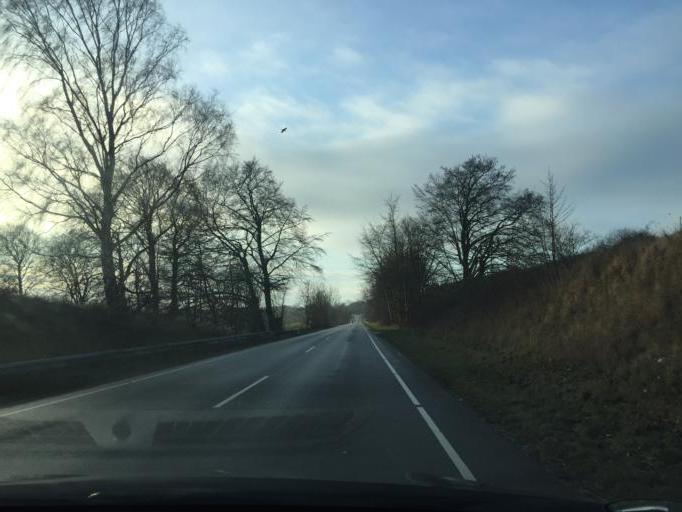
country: DK
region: South Denmark
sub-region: Faaborg-Midtfyn Kommune
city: Faaborg
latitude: 55.1620
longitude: 10.2744
